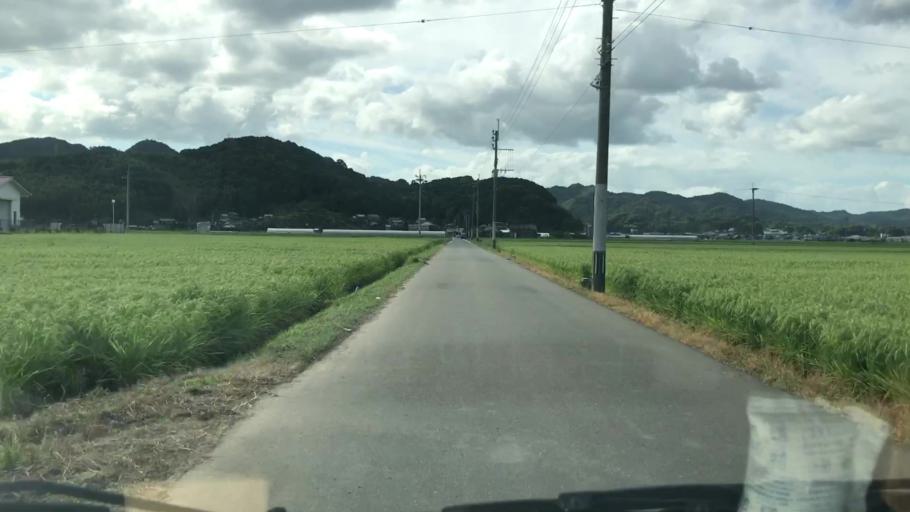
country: JP
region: Saga Prefecture
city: Kashima
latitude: 33.1156
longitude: 130.0771
